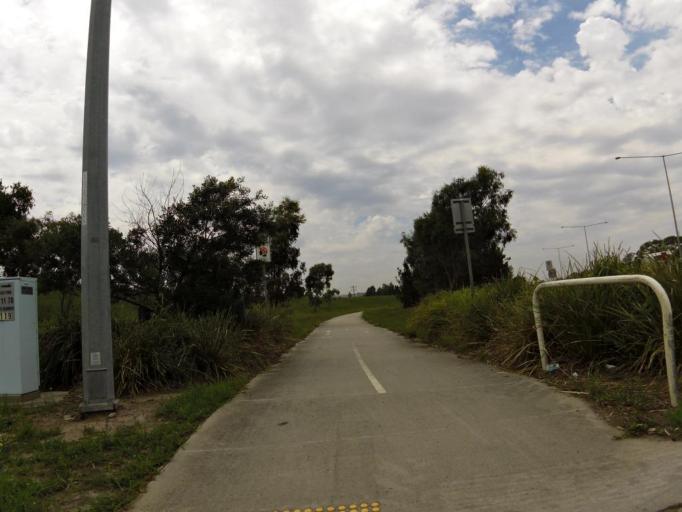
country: AU
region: Victoria
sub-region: Greater Dandenong
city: Keysborough
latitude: -37.9997
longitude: 145.1810
